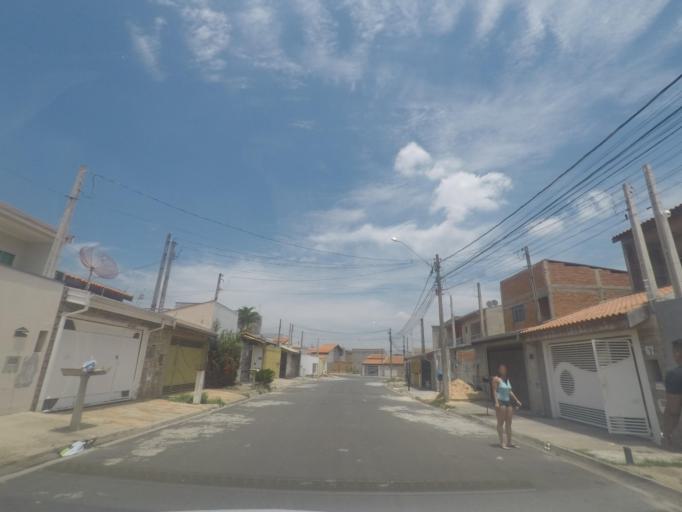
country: BR
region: Sao Paulo
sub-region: Sumare
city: Sumare
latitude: -22.8012
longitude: -47.2742
